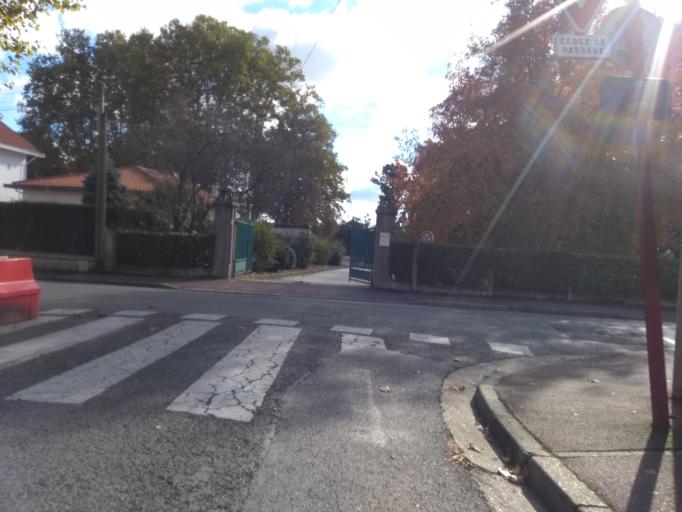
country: FR
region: Aquitaine
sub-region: Departement de la Gironde
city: Pessac
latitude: 44.8039
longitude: -0.6308
